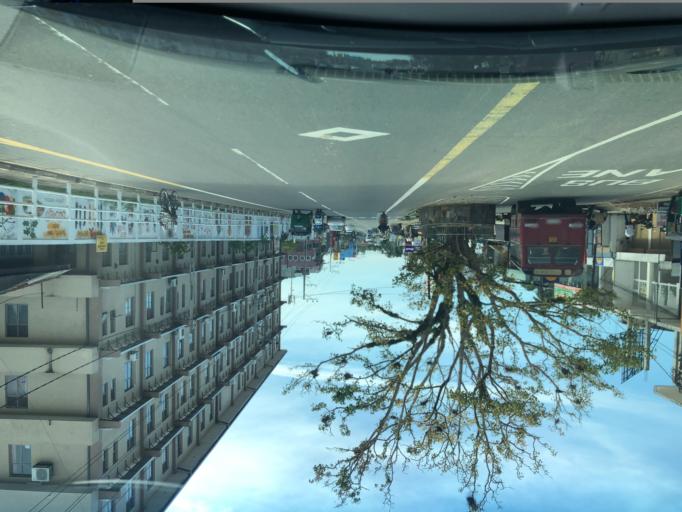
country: LK
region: Western
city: Kalutara
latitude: 6.5631
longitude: 79.9837
